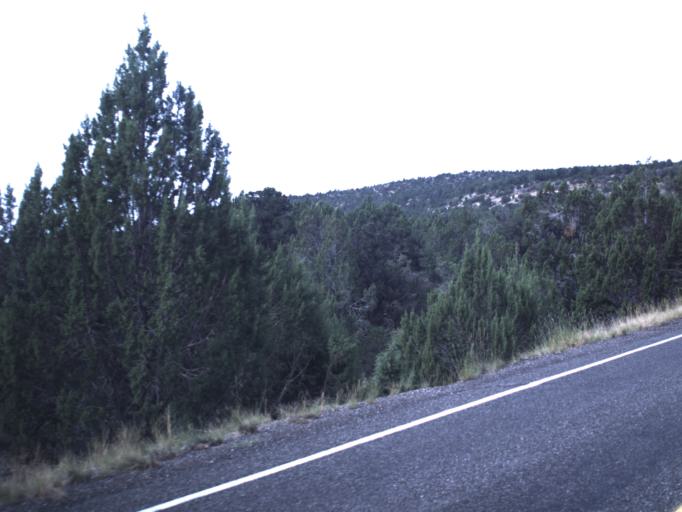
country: US
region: Utah
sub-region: Washington County
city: Hildale
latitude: 37.2621
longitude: -112.7874
